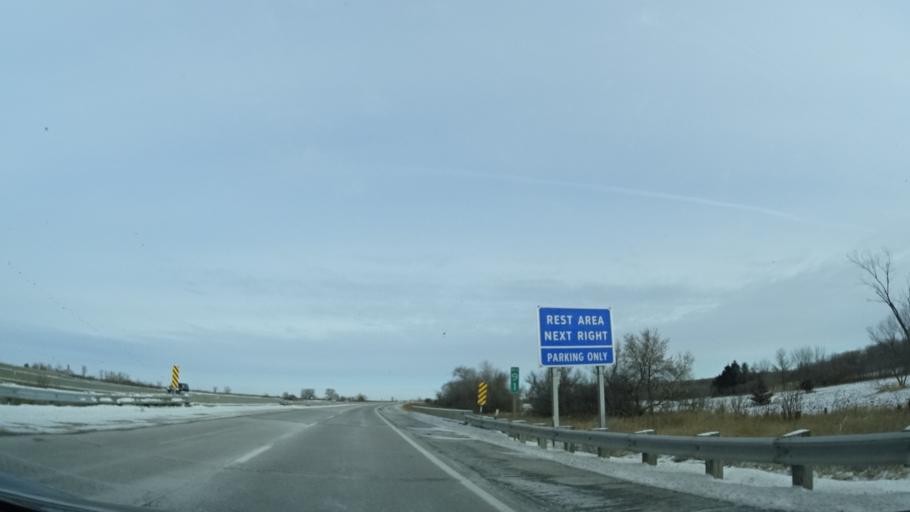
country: US
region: Nebraska
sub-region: Burt County
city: Tekamah
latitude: 41.7357
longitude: -96.0482
